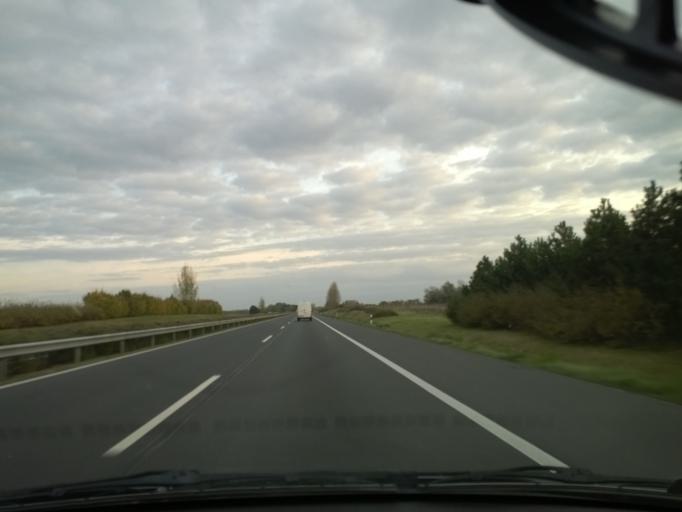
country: HU
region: Bacs-Kiskun
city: Varosfoeld
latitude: 46.7850
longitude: 19.7476
